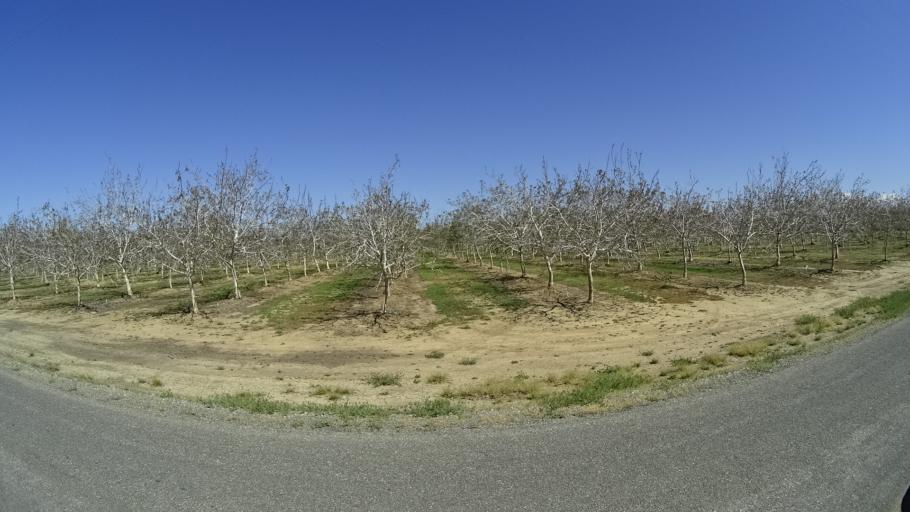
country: US
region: California
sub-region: Glenn County
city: Orland
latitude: 39.6963
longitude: -122.1559
